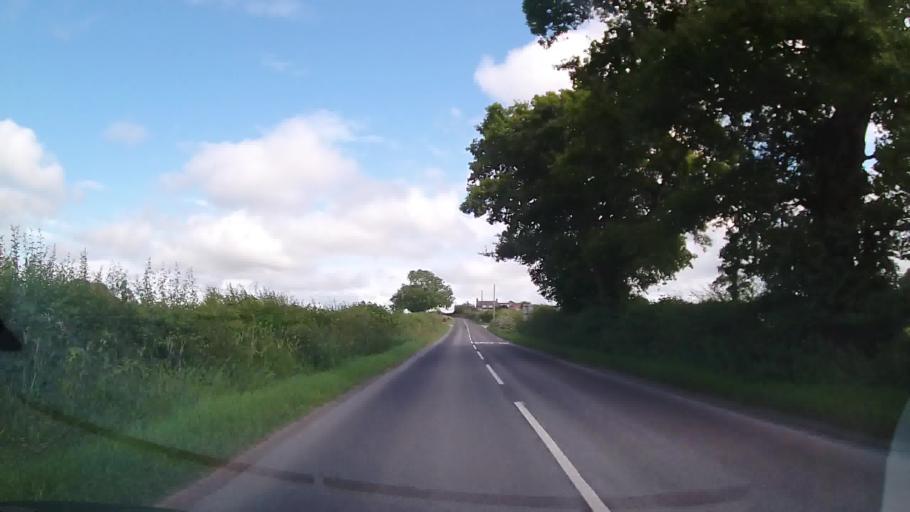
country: GB
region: England
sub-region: Shropshire
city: Pant
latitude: 52.8017
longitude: -3.0191
